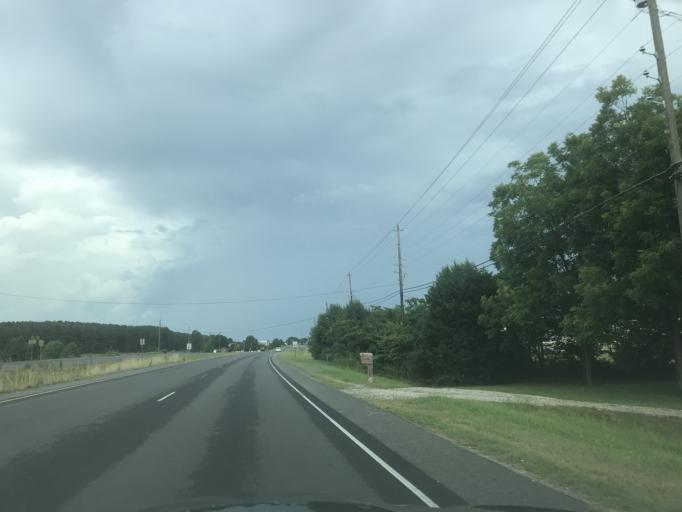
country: US
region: North Carolina
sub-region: Johnston County
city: Clayton
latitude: 35.6323
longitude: -78.4357
